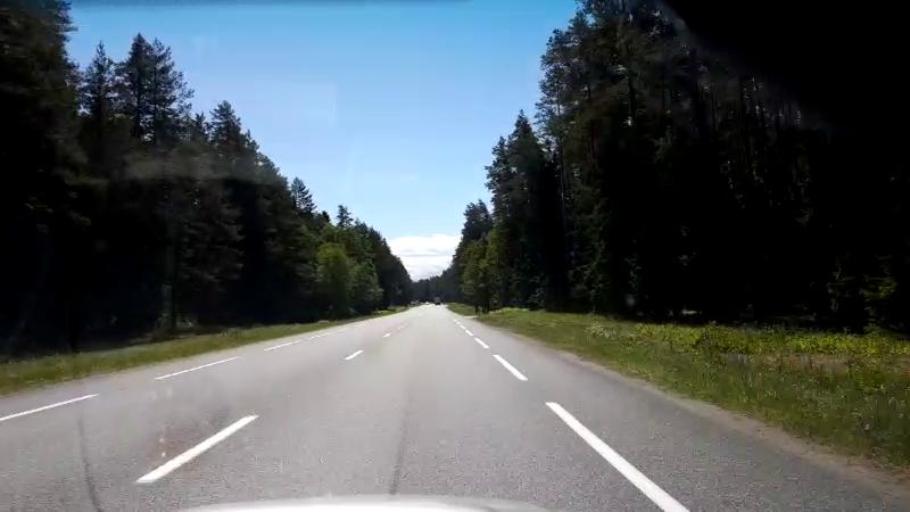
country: LV
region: Saulkrastu
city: Saulkrasti
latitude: 57.3531
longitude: 24.4384
